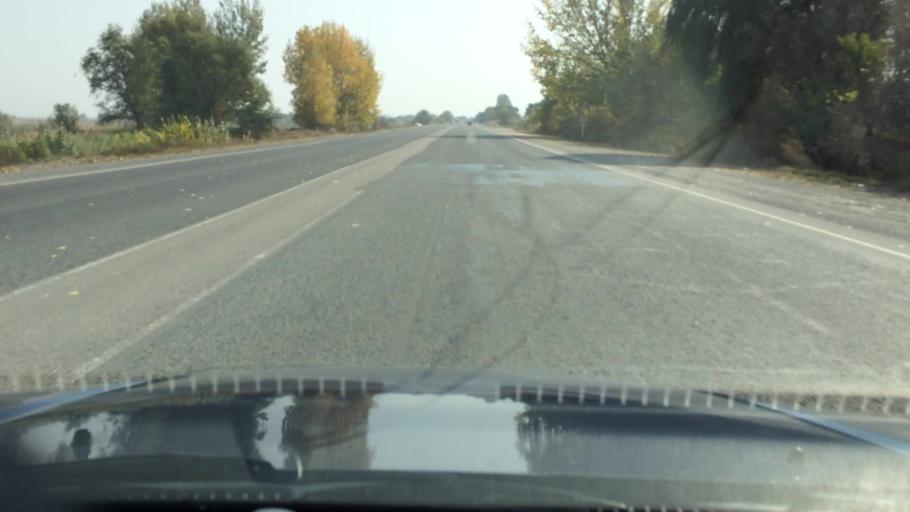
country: KG
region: Chuy
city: Kant
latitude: 42.9462
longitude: 74.9589
